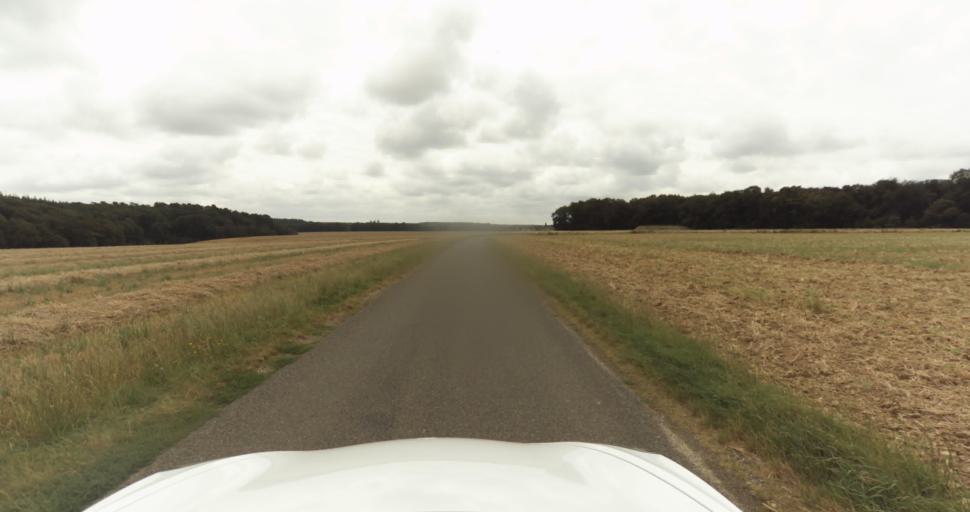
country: FR
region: Haute-Normandie
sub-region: Departement de l'Eure
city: Saint-Sebastien-de-Morsent
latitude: 49.0267
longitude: 1.0619
